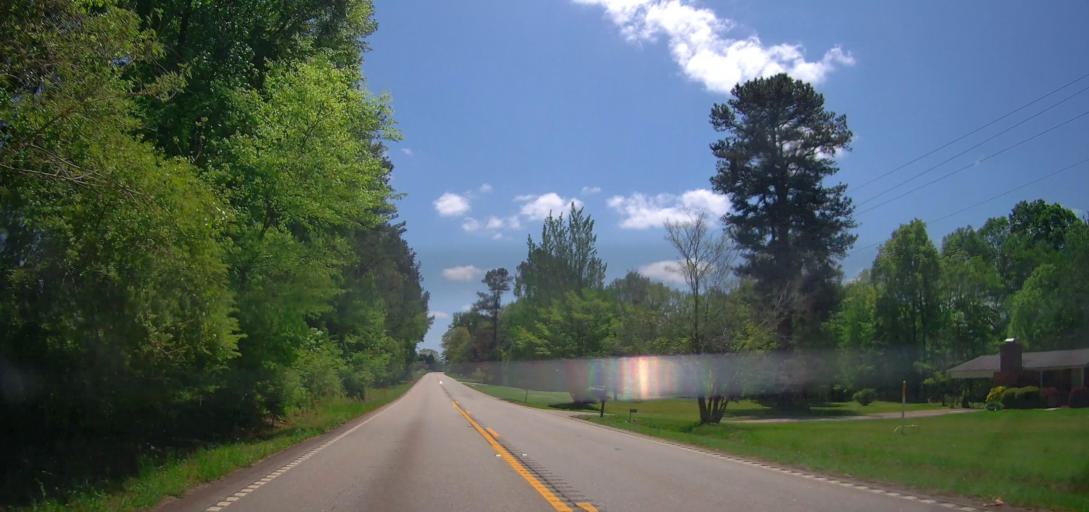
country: US
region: Georgia
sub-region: Jasper County
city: Monticello
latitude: 33.1880
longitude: -83.6468
